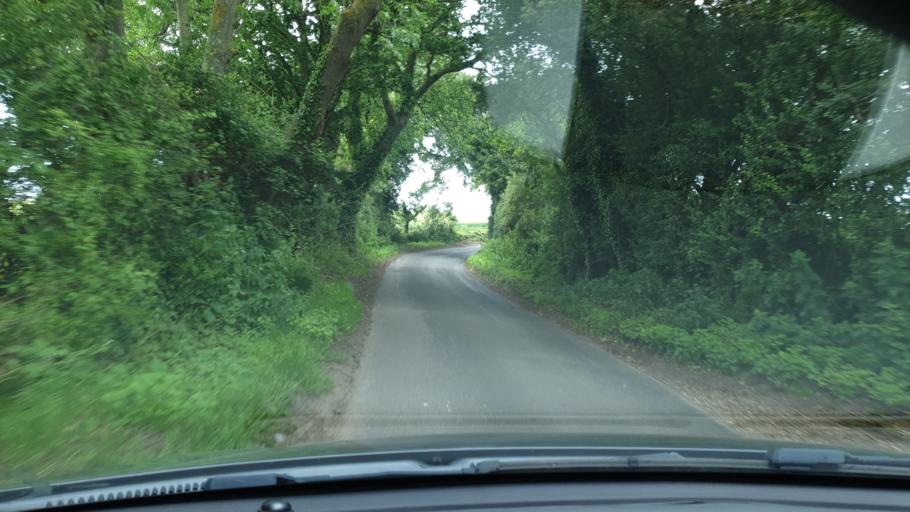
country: GB
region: England
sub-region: Suffolk
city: Shotley Gate
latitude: 51.9189
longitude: 1.2045
